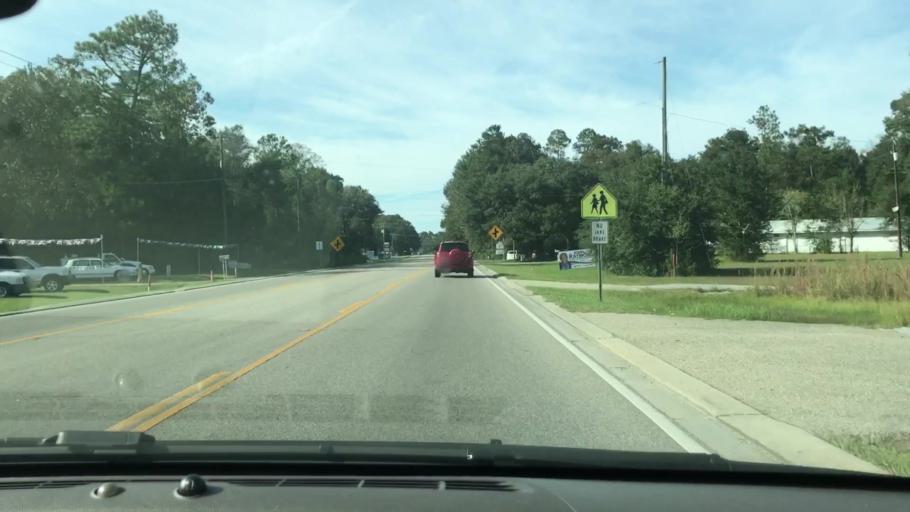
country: US
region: Louisiana
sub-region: Saint Tammany Parish
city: Pearl River
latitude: 30.3672
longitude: -89.7592
